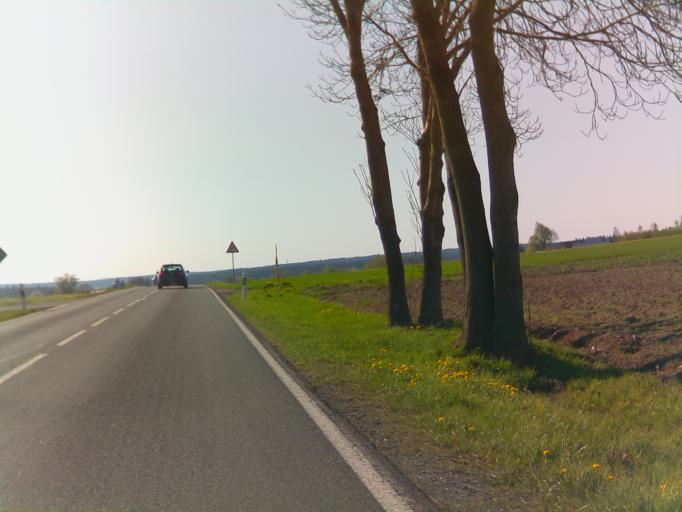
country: DE
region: Thuringia
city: Dreba
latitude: 50.6909
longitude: 11.7746
